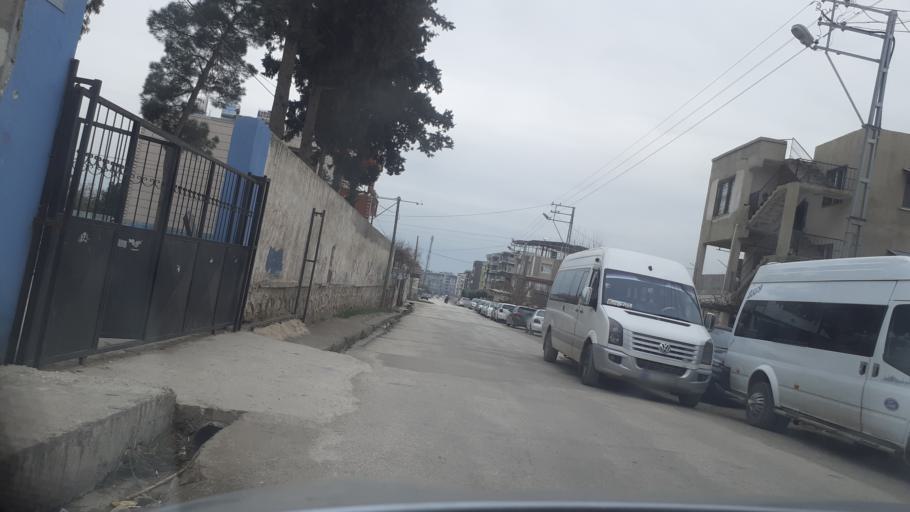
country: TR
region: Hatay
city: Kirikhan
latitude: 36.4873
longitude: 36.3557
